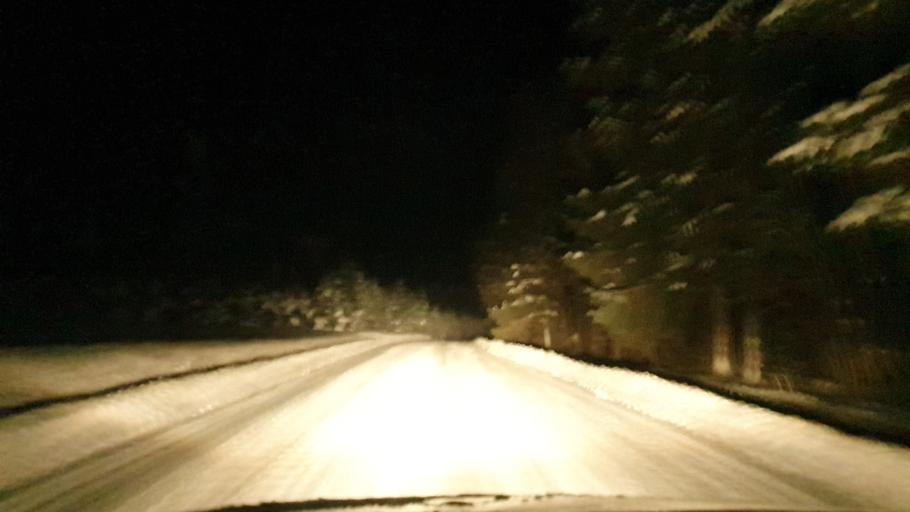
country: EE
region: Vorumaa
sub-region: Antsla vald
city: Vana-Antsla
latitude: 57.9495
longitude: 26.6371
